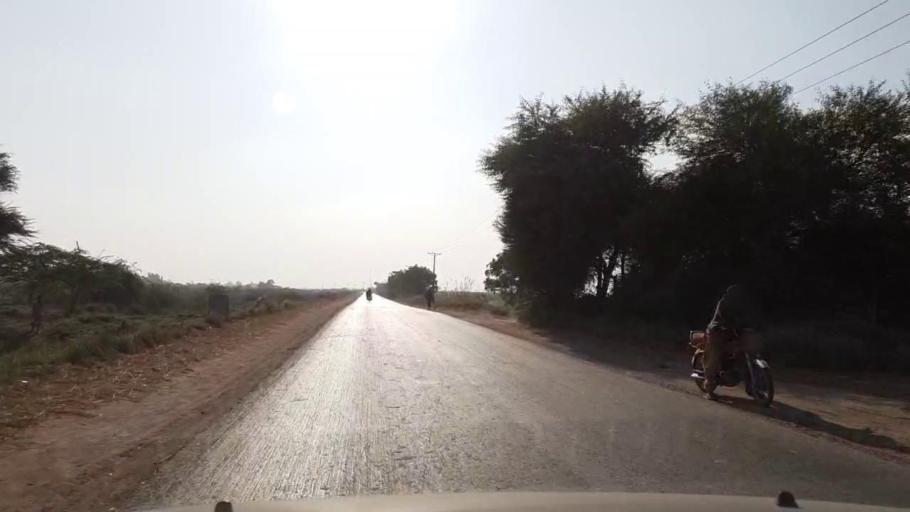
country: PK
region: Sindh
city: Bulri
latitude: 25.0060
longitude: 68.3973
